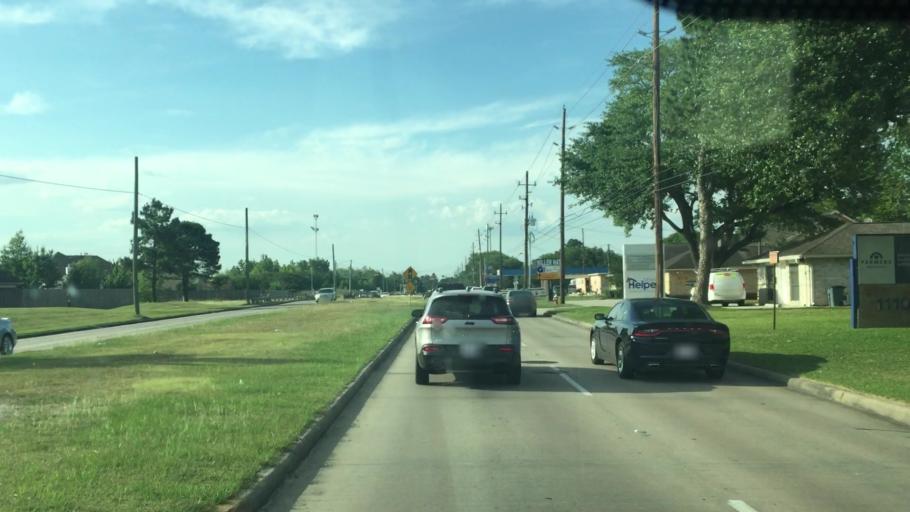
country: US
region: Texas
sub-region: Harris County
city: Hudson
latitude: 29.9547
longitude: -95.4983
